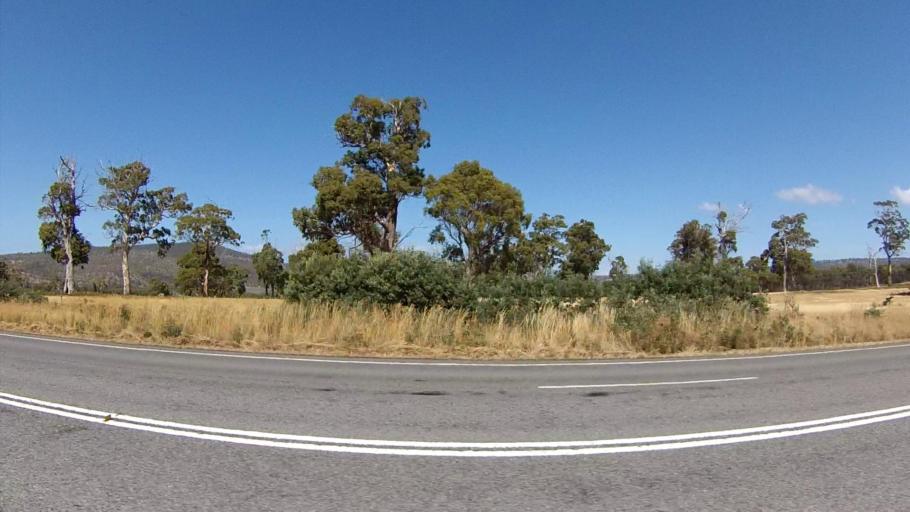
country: AU
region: Tasmania
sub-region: Sorell
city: Sorell
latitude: -42.5981
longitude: 147.7654
